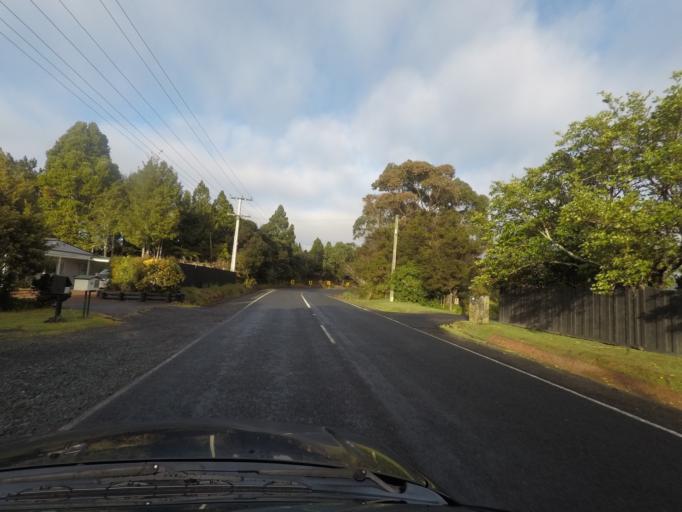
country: NZ
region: Auckland
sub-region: Auckland
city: Waitakere
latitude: -36.9129
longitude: 174.6055
